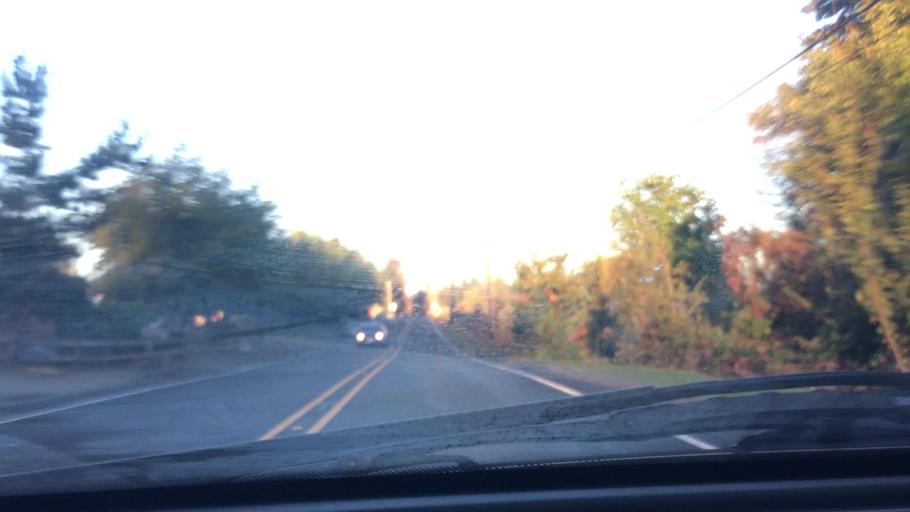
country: US
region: Oregon
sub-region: Washington County
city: Sherwood
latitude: 45.3606
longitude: -122.8268
